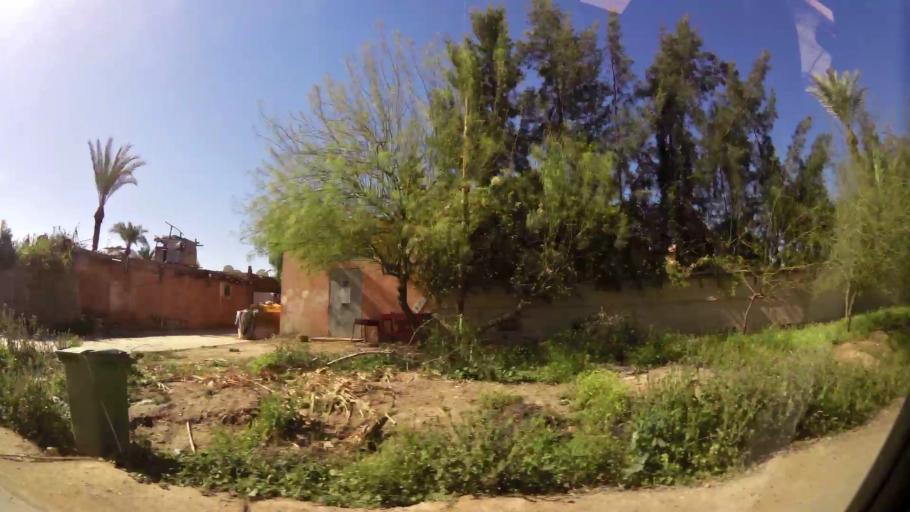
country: MA
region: Marrakech-Tensift-Al Haouz
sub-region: Marrakech
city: Marrakesh
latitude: 31.6722
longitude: -7.9571
